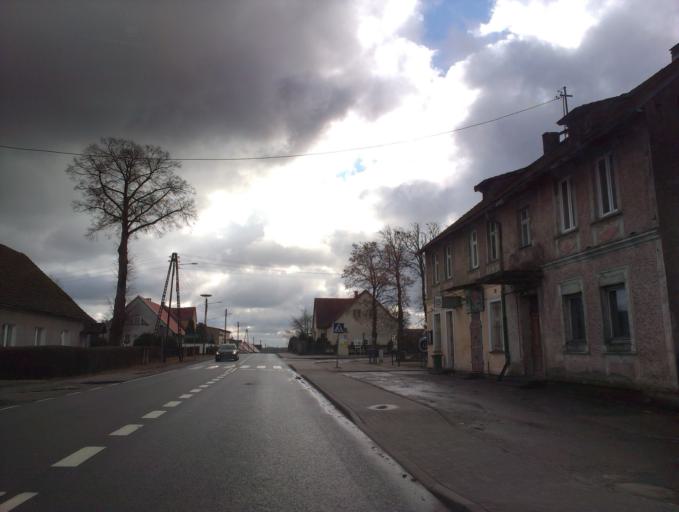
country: PL
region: West Pomeranian Voivodeship
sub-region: Powiat szczecinecki
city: Szczecinek
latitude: 53.7365
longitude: 16.8002
